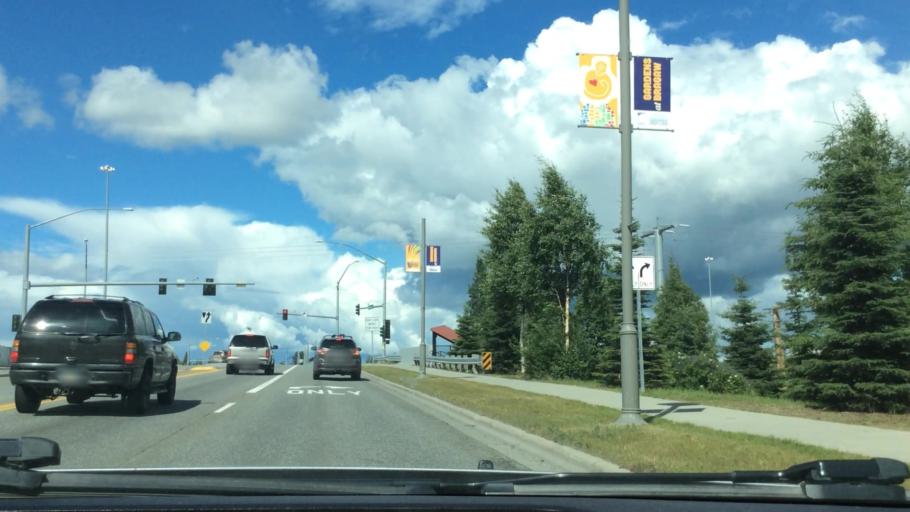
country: US
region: Alaska
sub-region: Anchorage Municipality
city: Anchorage
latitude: 61.2198
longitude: -149.8082
